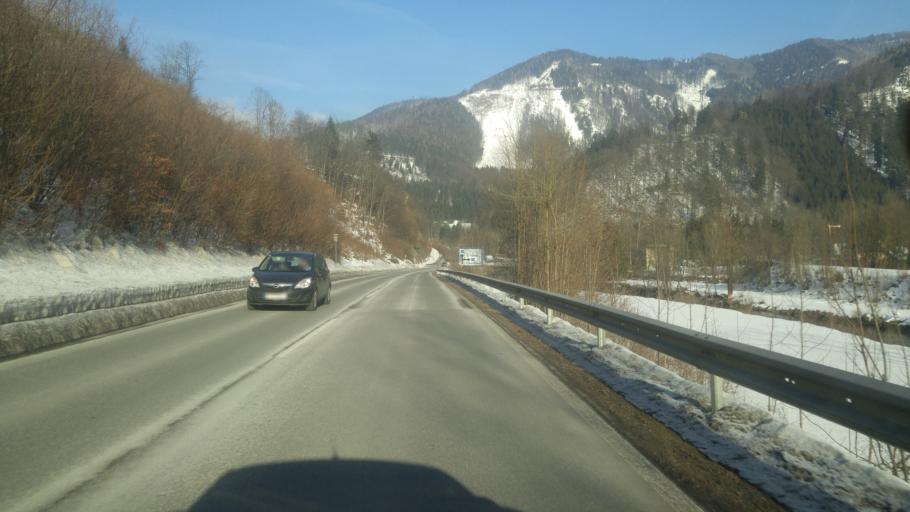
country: AT
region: Lower Austria
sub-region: Politischer Bezirk Lilienfeld
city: Lilienfeld
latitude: 47.9739
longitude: 15.5663
